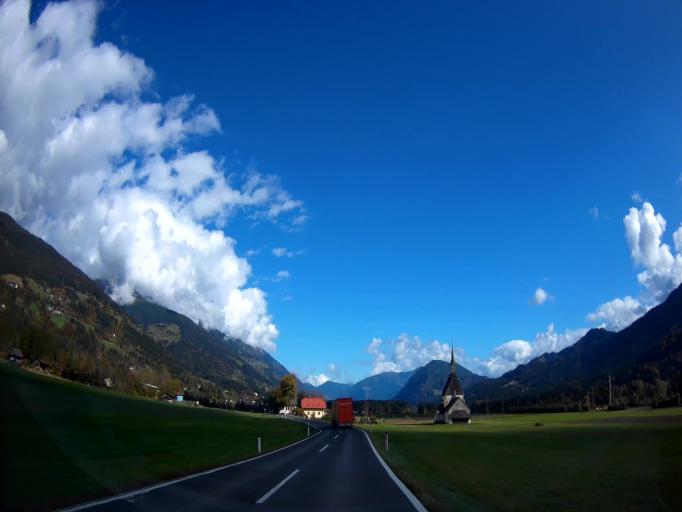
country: AT
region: Carinthia
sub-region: Politischer Bezirk Spittal an der Drau
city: Berg im Drautal
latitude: 46.7396
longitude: 13.1406
